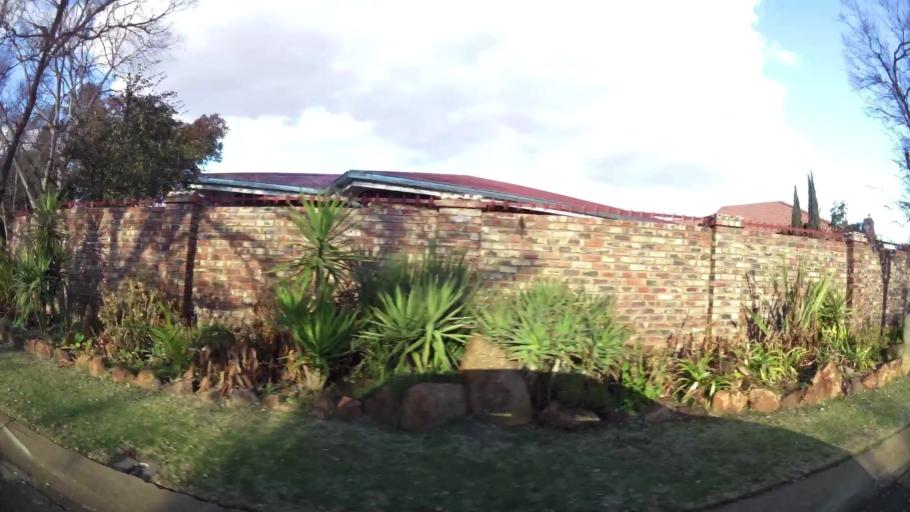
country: ZA
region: North-West
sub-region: Dr Kenneth Kaunda District Municipality
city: Potchefstroom
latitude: -26.7208
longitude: 27.0828
